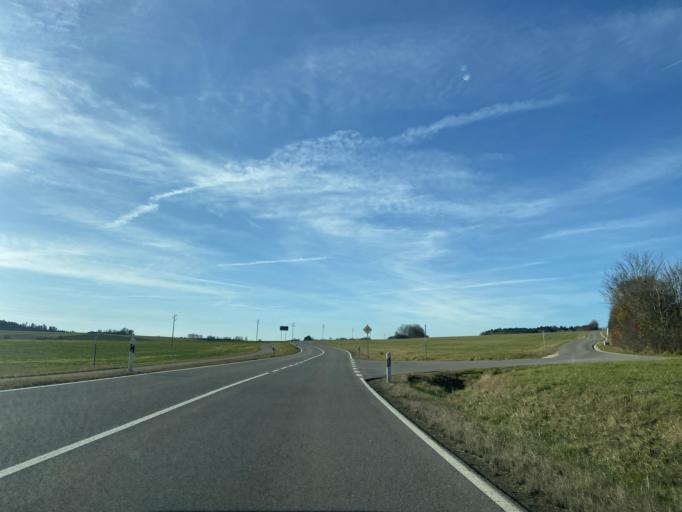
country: DE
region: Baden-Wuerttemberg
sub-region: Tuebingen Region
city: Stetten am Kalten Markt
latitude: 48.1210
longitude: 9.0640
